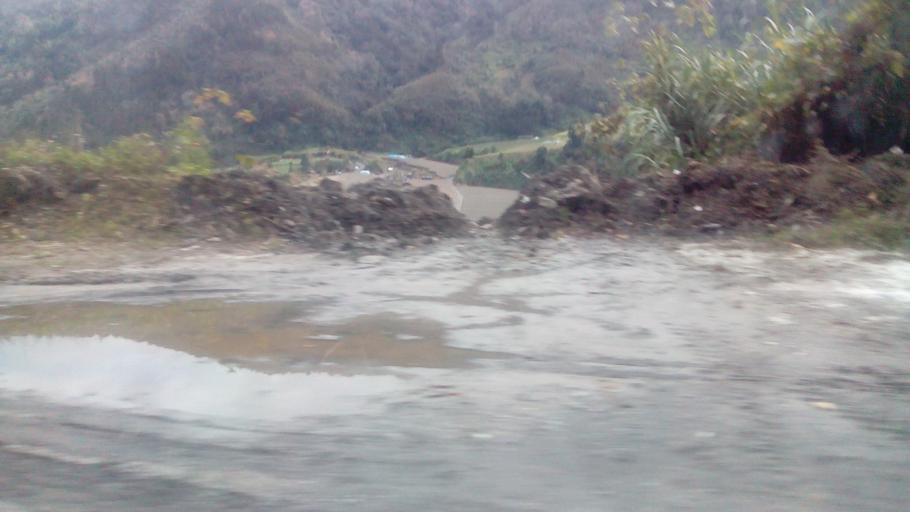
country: TW
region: Taiwan
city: Daxi
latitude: 24.4516
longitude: 121.3899
